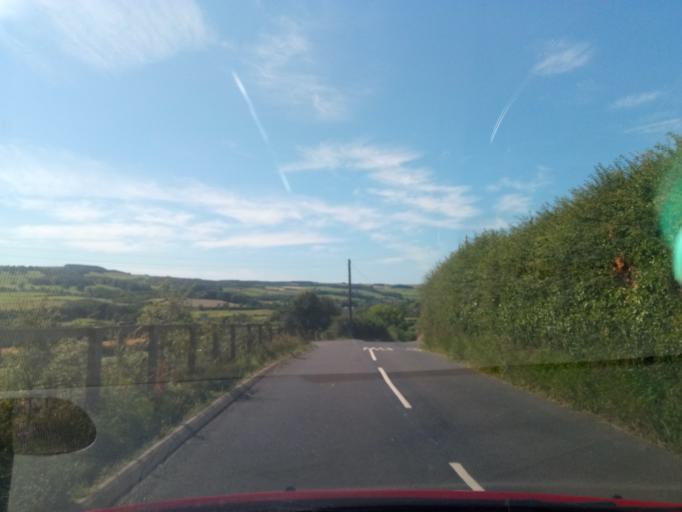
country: GB
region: England
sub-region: Northumberland
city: Warden
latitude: 54.9810
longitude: -2.2292
